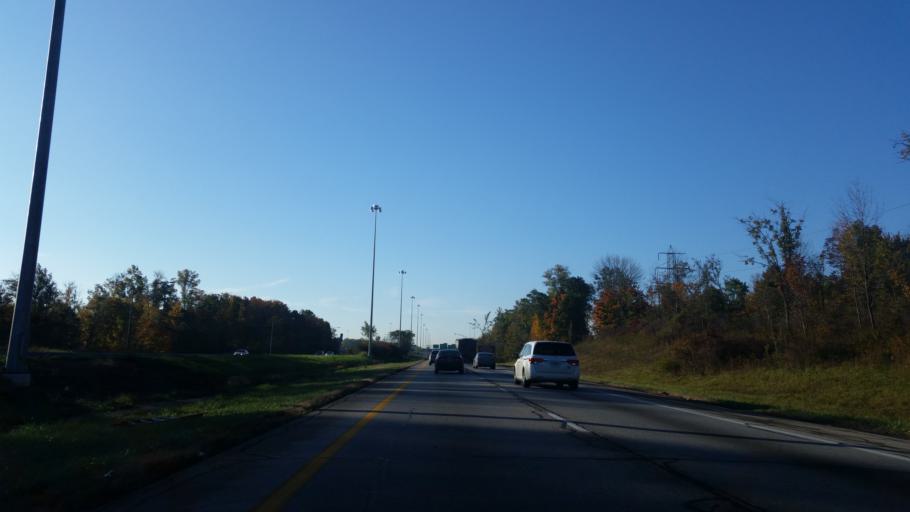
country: US
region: Ohio
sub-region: Summit County
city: Richfield
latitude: 41.2377
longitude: -81.6284
